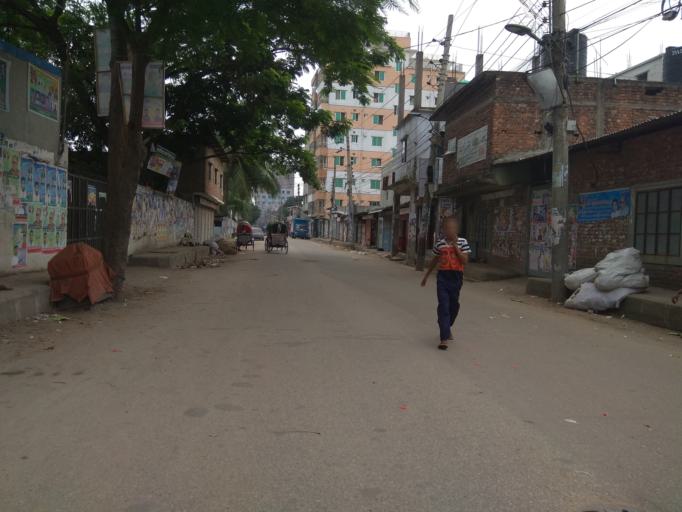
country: BD
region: Dhaka
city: Azimpur
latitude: 23.7119
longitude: 90.3704
